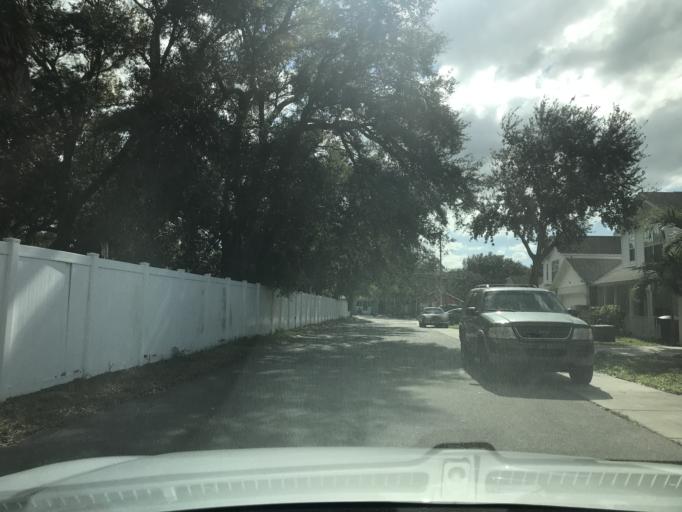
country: US
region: Florida
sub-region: Pinellas County
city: Belleair
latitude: 27.9433
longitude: -82.7905
